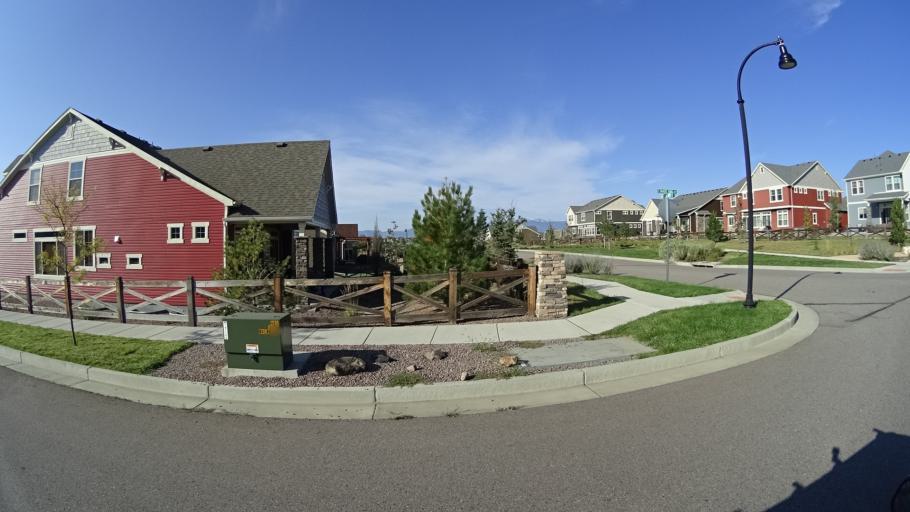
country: US
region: Colorado
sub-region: El Paso County
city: Cimarron Hills
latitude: 38.9344
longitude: -104.6685
